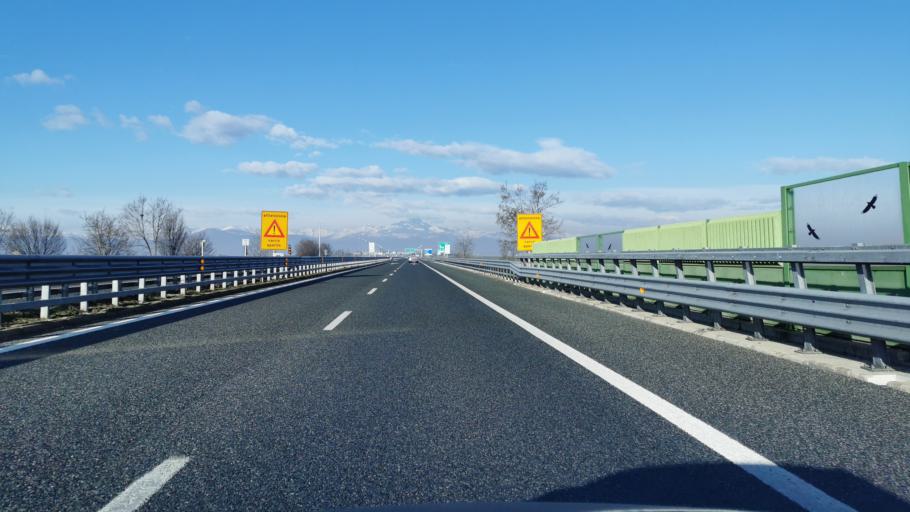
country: IT
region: Piedmont
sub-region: Provincia di Cuneo
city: Montanera
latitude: 44.4734
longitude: 7.7024
